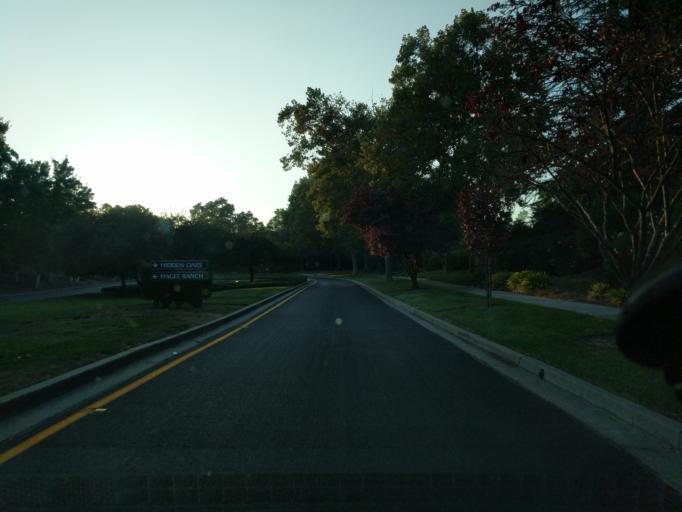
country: US
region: California
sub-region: Contra Costa County
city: Diablo
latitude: 37.8275
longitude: -121.9365
